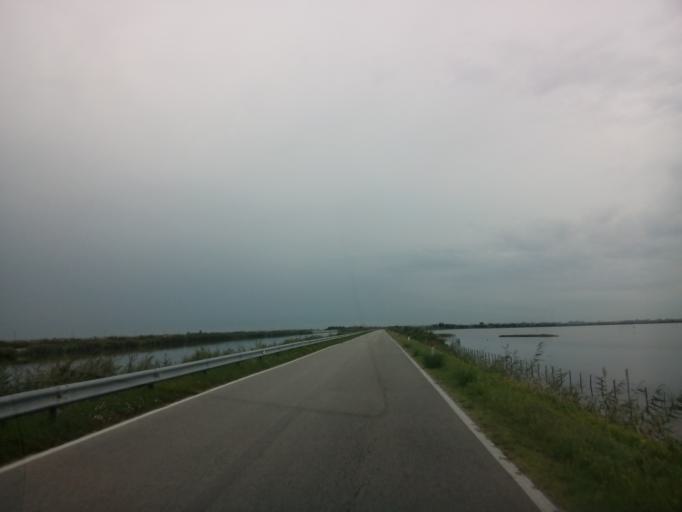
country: IT
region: Veneto
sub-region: Provincia di Rovigo
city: Rosolina
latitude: 45.0469
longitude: 12.3191
